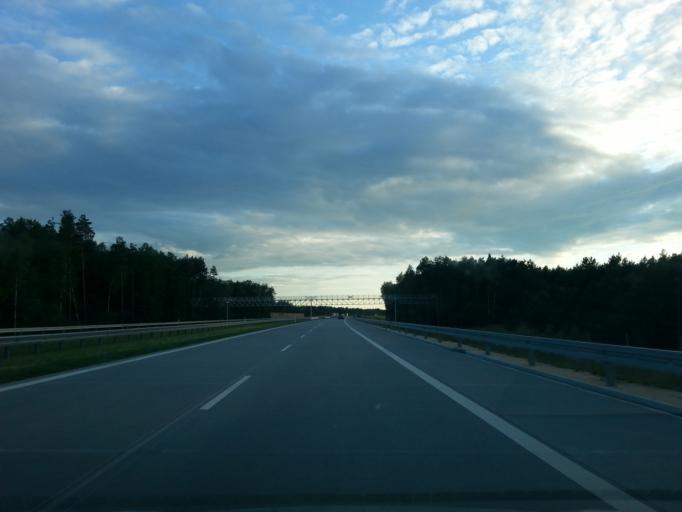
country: PL
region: Lodz Voivodeship
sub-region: Powiat wieruszowski
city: Lututow
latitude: 51.3402
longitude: 18.4942
